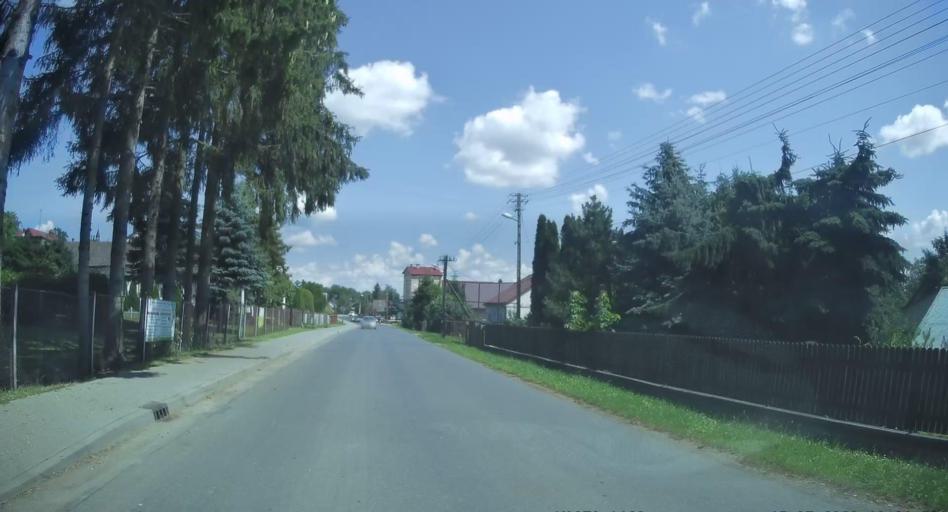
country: PL
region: Subcarpathian Voivodeship
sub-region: Powiat przemyski
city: Medyka
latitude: 49.8396
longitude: 22.8838
